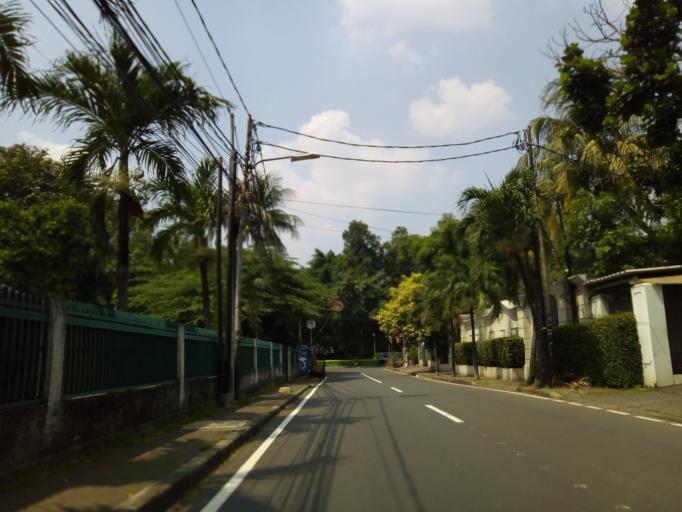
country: ID
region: Jakarta Raya
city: Jakarta
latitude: -6.2026
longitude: 106.8410
